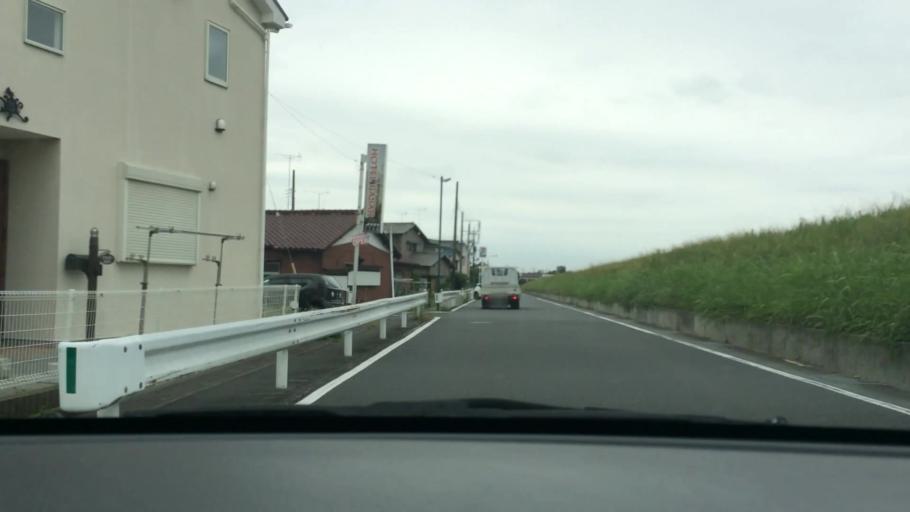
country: JP
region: Chiba
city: Matsudo
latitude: 35.7899
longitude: 139.8872
